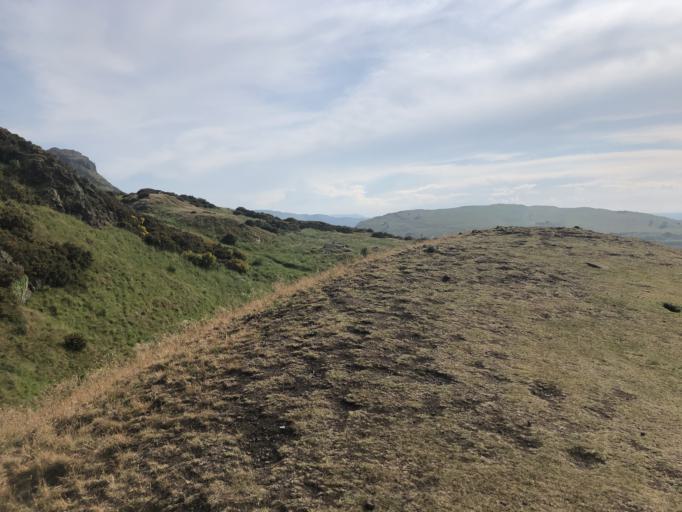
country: GB
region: Scotland
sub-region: West Lothian
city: Seafield
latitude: 55.9506
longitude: -3.1579
